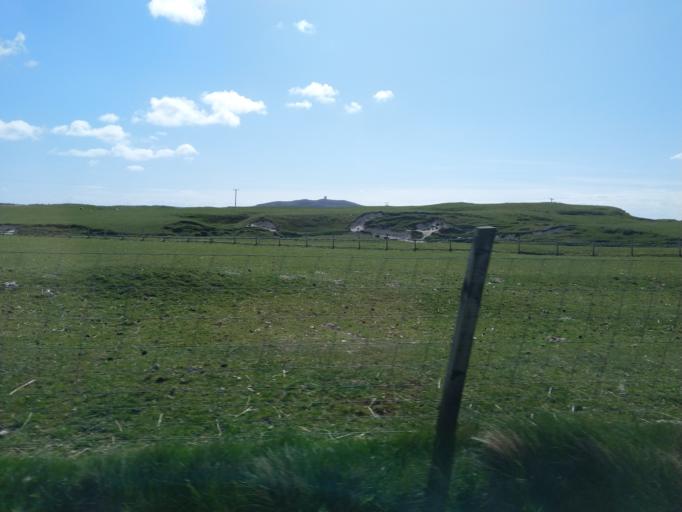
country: GB
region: Scotland
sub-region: Eilean Siar
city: Barra
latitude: 56.4823
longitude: -6.8870
